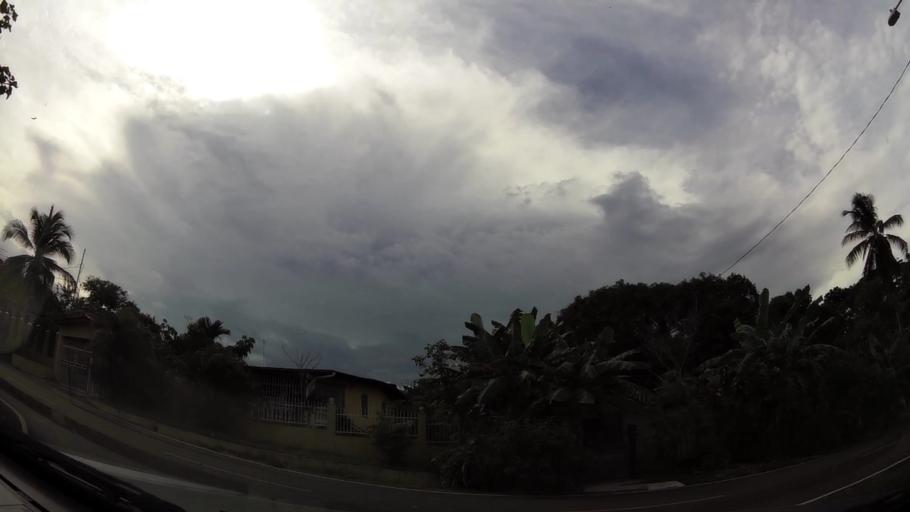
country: PA
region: Panama
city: El Coco
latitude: 8.8653
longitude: -79.8093
